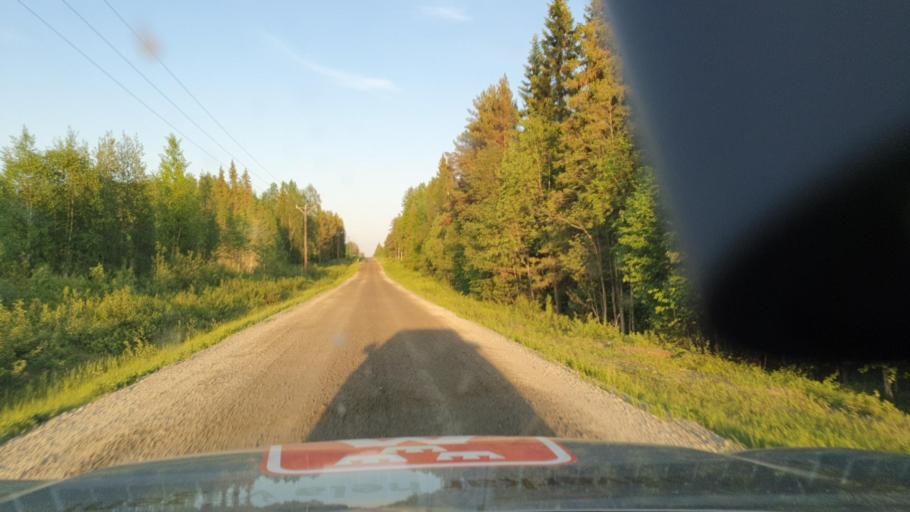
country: SE
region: Norrbotten
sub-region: Bodens Kommun
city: Boden
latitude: 66.0733
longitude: 21.7020
